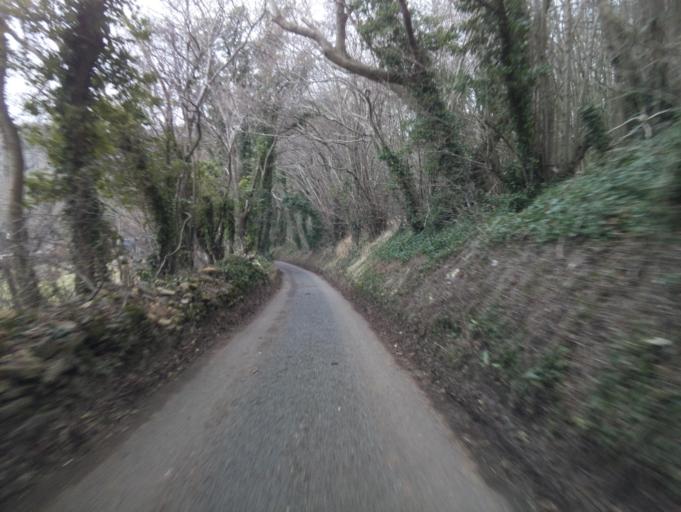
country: GB
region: England
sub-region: Wiltshire
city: Biddestone
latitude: 51.4596
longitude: -2.2255
